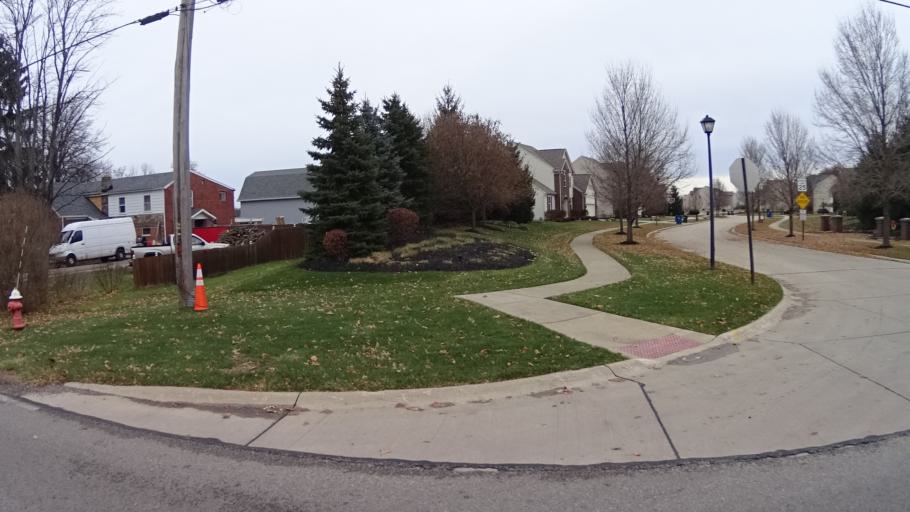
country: US
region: Ohio
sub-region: Lorain County
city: North Ridgeville
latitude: 41.3565
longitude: -82.0033
